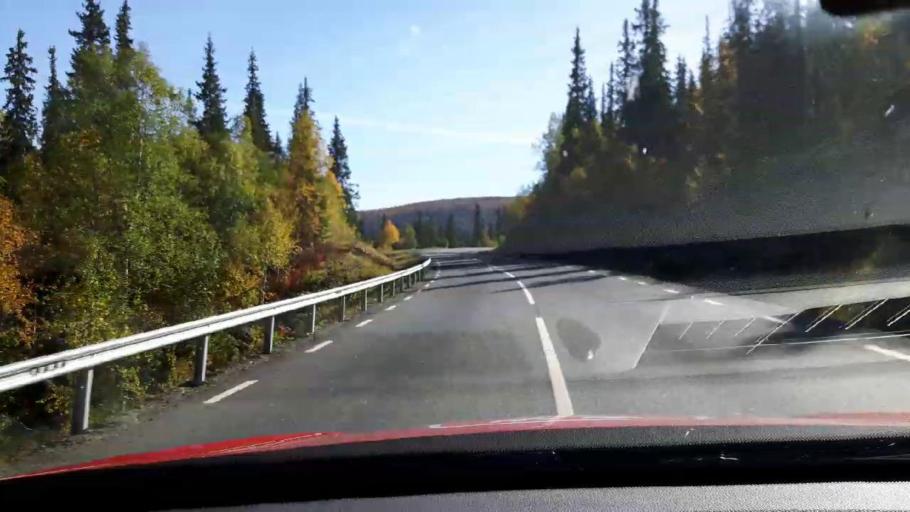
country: NO
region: Nord-Trondelag
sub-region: Royrvik
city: Royrvik
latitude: 64.8576
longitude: 14.1800
